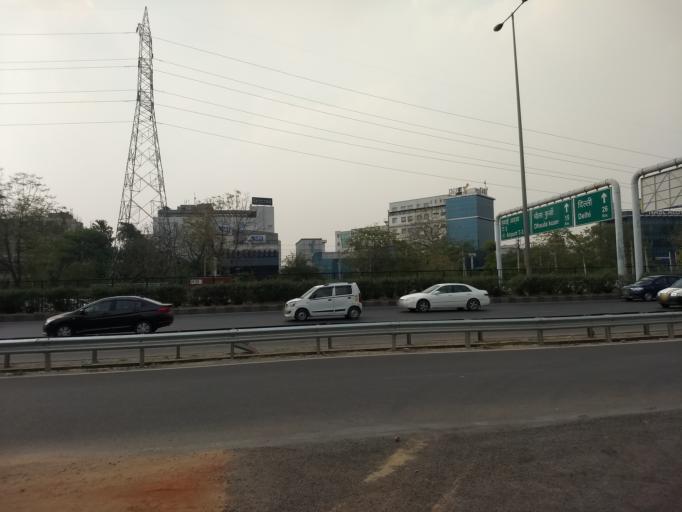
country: IN
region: Haryana
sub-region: Gurgaon
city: Gurgaon
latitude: 28.4913
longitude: 77.0827
